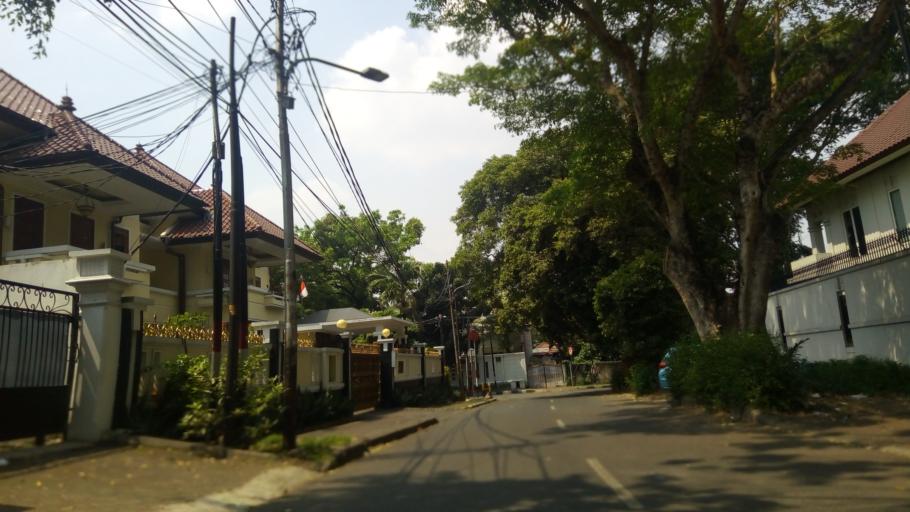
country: ID
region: Jakarta Raya
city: Jakarta
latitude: -6.2018
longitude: 106.8299
